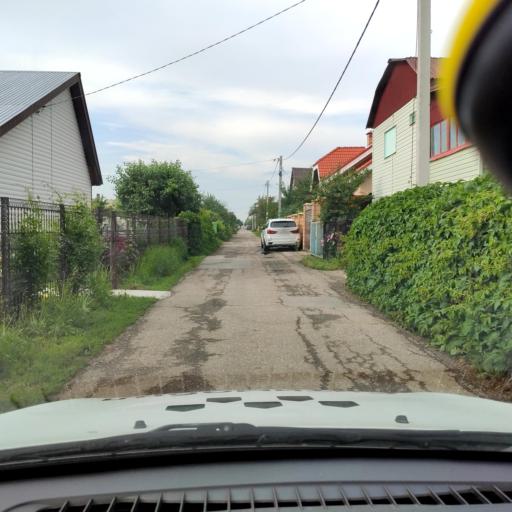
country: RU
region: Samara
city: Podstepki
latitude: 53.5762
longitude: 49.0789
